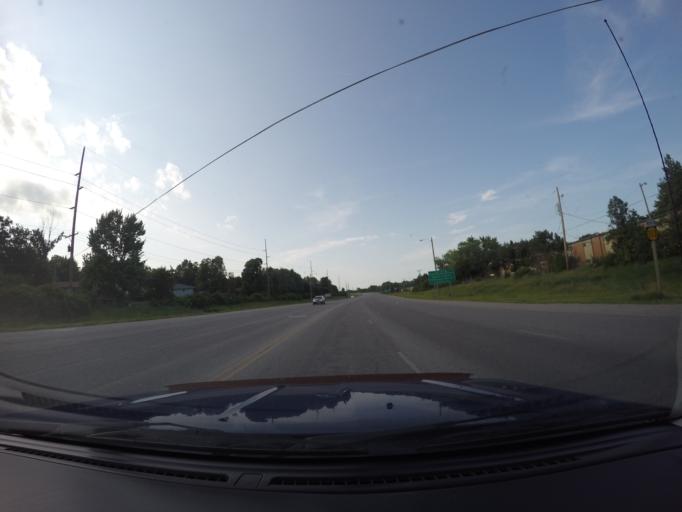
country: US
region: Kansas
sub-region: Riley County
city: Manhattan
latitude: 39.1931
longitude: -96.6124
